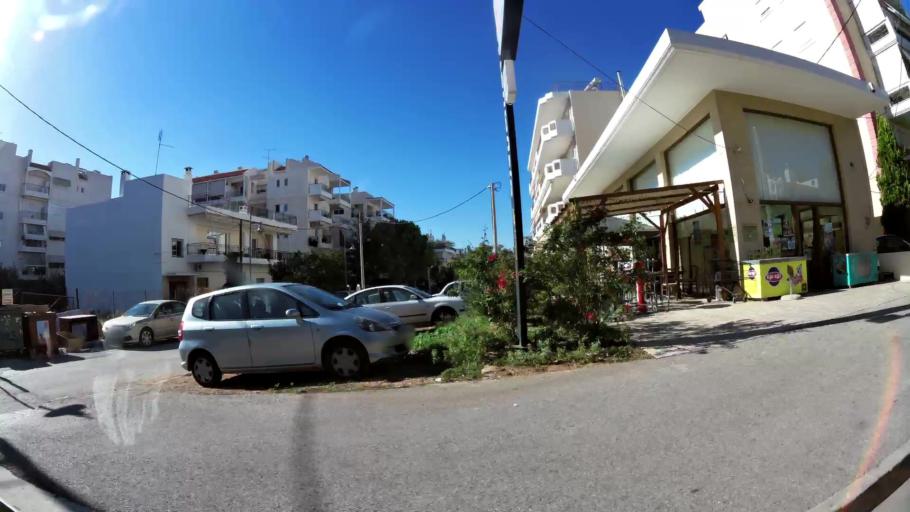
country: GR
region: Attica
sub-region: Nomarchia Athinas
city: Vrilissia
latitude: 38.0312
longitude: 23.8381
